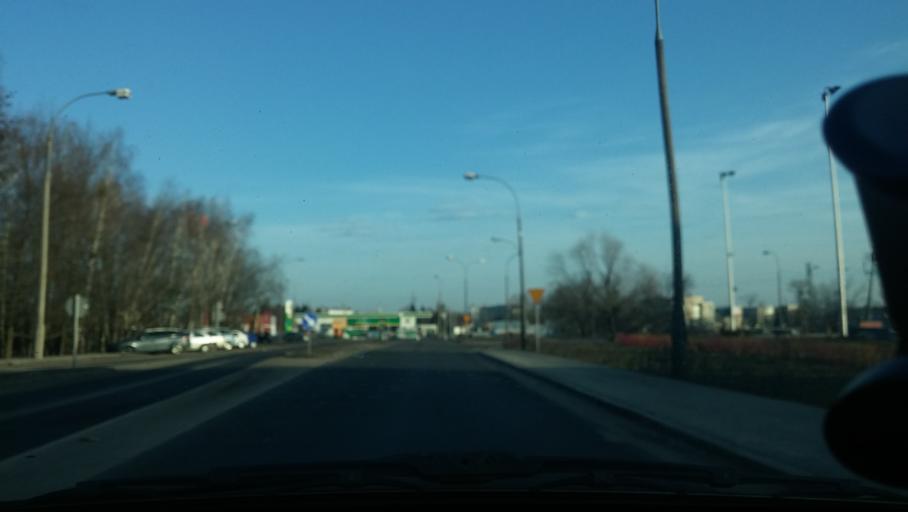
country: PL
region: Masovian Voivodeship
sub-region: Powiat piaseczynski
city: Piaseczno
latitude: 52.0801
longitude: 21.0215
